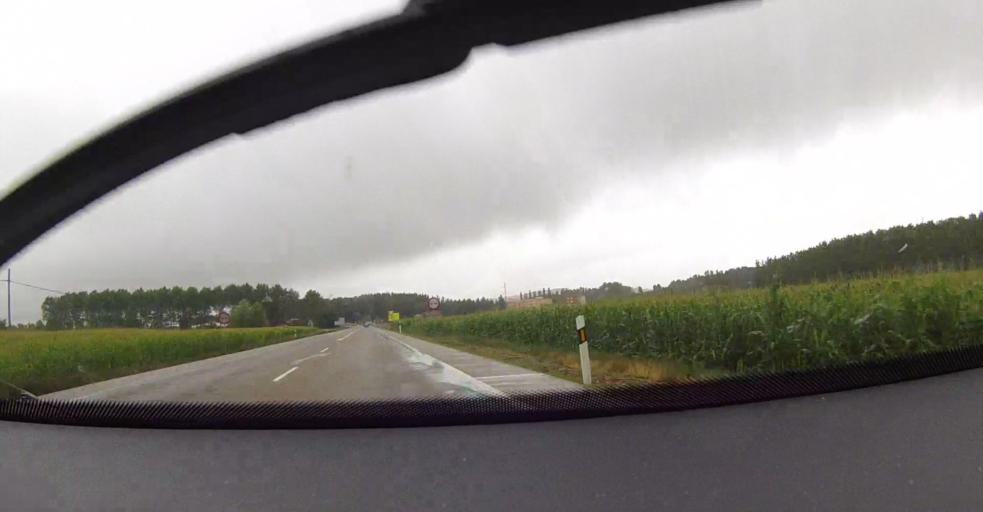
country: ES
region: Castille and Leon
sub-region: Provincia de Palencia
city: Saldana
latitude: 42.5104
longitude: -4.7379
